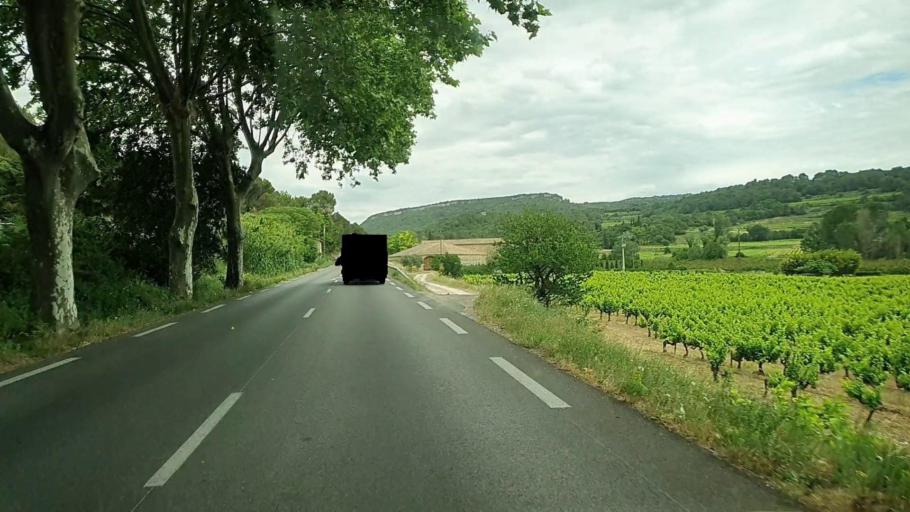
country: FR
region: Languedoc-Roussillon
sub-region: Departement du Gard
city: Tresques
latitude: 44.1072
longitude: 4.6104
